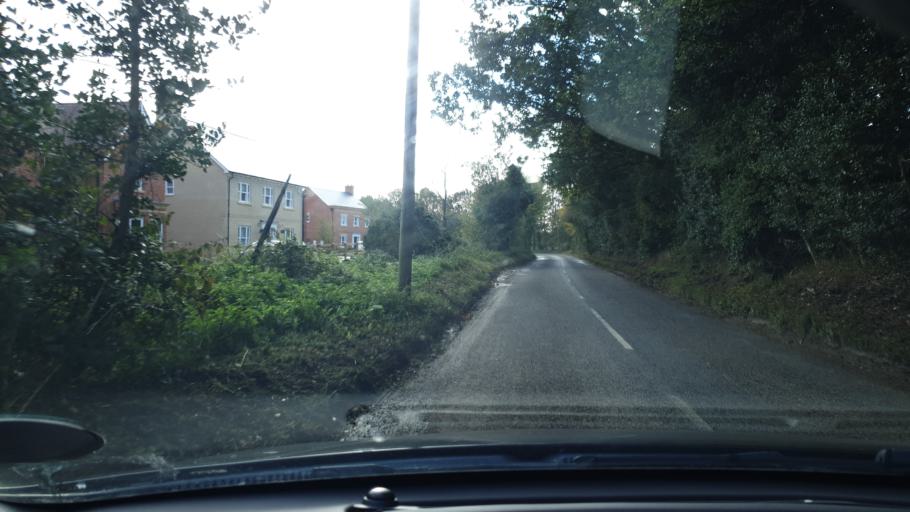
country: GB
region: England
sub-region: Essex
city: Manningtree
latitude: 51.9353
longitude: 1.0454
